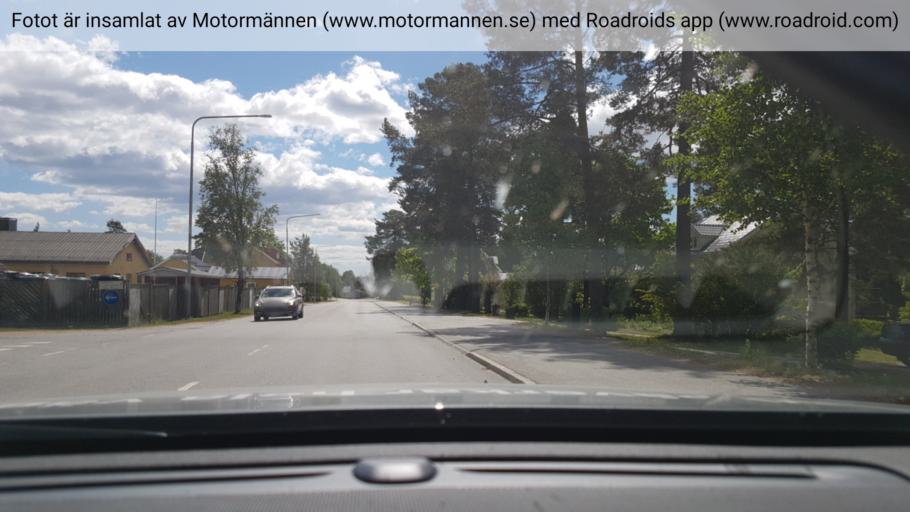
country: SE
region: Vaesterbotten
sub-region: Nordmalings Kommun
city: Nordmaling
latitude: 63.5760
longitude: 19.4881
